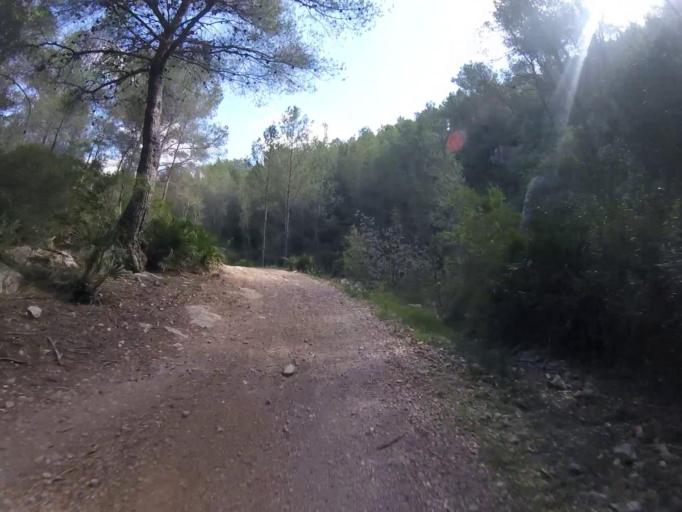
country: ES
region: Valencia
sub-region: Provincia de Castello
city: Alcoceber
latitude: 40.2982
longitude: 0.3150
